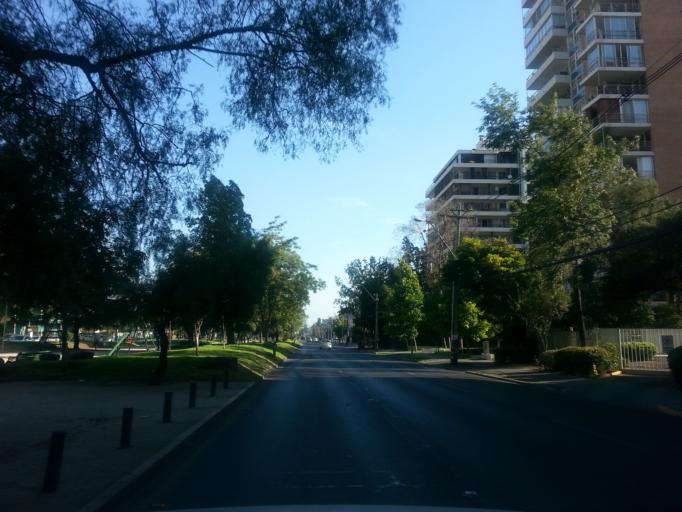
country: CL
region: Santiago Metropolitan
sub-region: Provincia de Santiago
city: Villa Presidente Frei, Nunoa, Santiago, Chile
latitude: -33.4286
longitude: -70.5752
